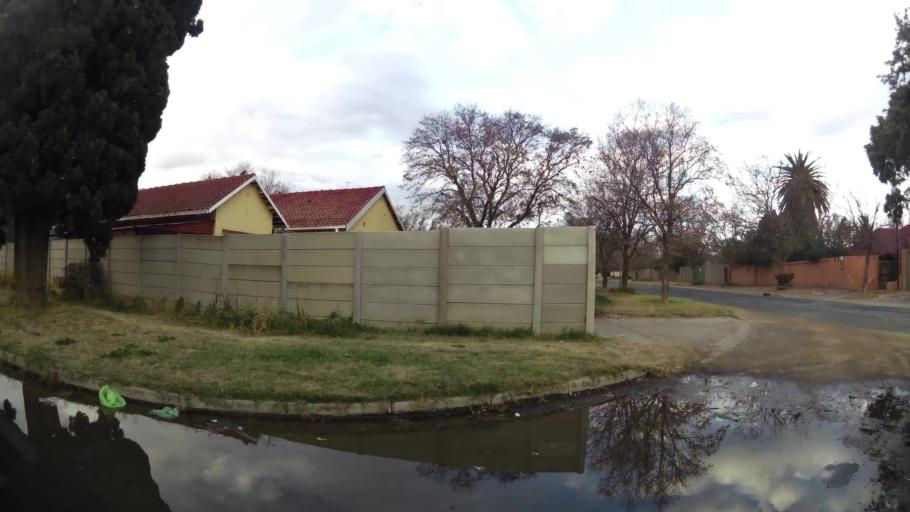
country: ZA
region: Orange Free State
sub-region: Lejweleputswa District Municipality
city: Welkom
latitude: -27.9816
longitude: 26.7248
